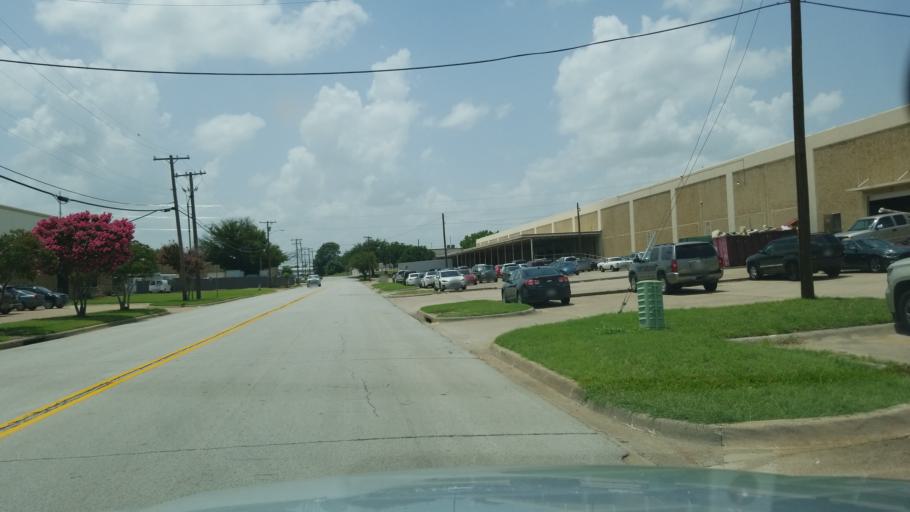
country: US
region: Texas
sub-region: Dallas County
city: Irving
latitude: 32.8185
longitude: -96.9140
